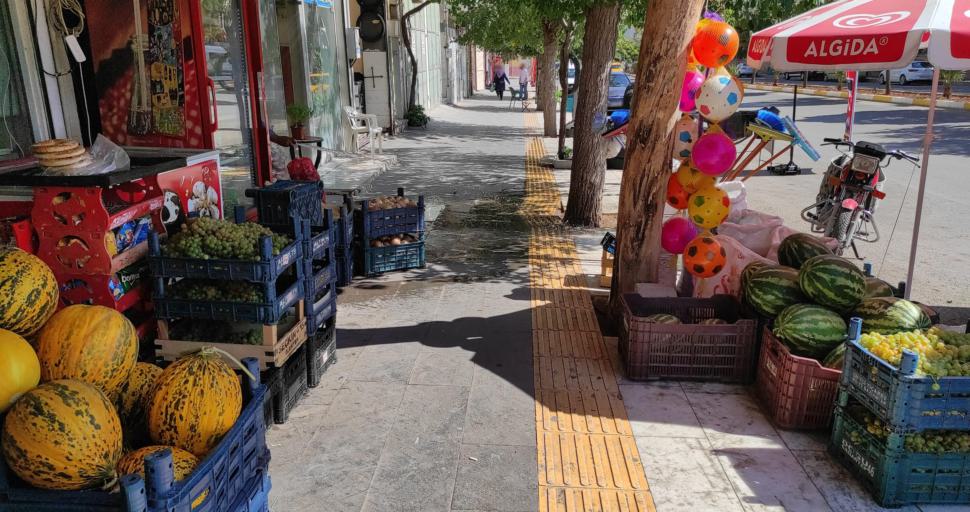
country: TR
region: Kilis
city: Kilis
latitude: 36.7236
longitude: 37.1051
